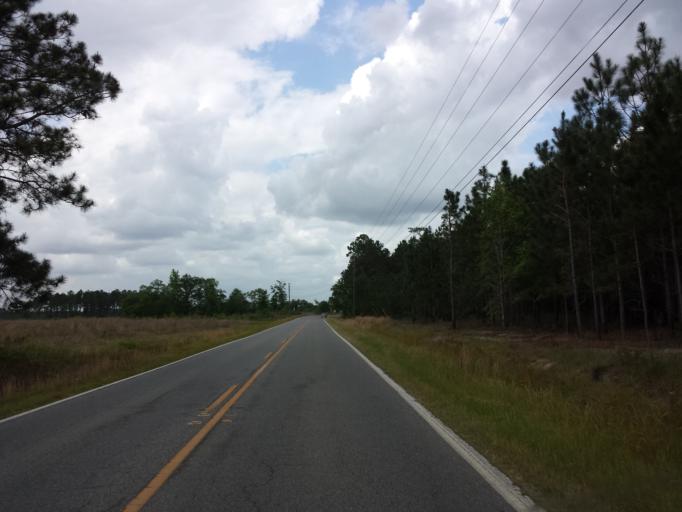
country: US
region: Georgia
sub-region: Cook County
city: Adel
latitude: 31.0814
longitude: -83.4030
